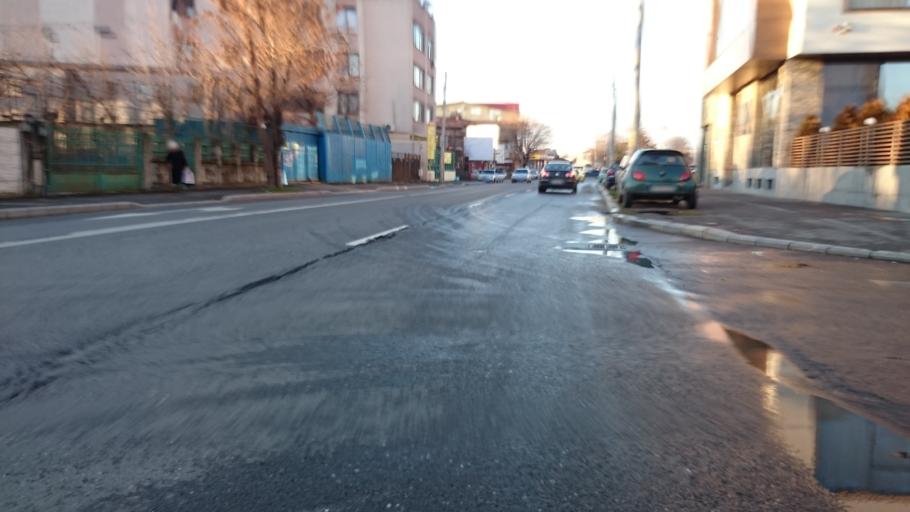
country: RO
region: Bucuresti
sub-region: Municipiul Bucuresti
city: Bucuresti
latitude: 44.4163
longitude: 26.0597
